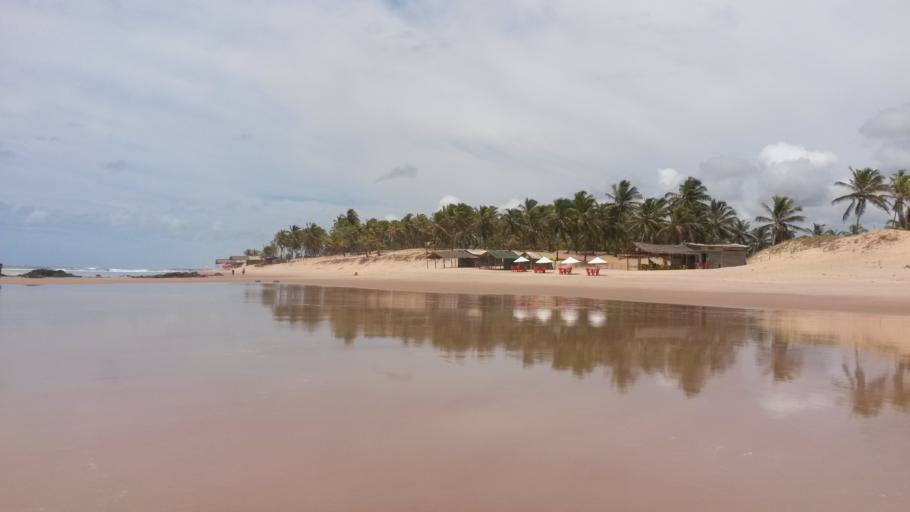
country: BR
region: Bahia
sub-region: Mata De Sao Joao
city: Mata de Sao Joao
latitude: -12.4586
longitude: -37.9314
